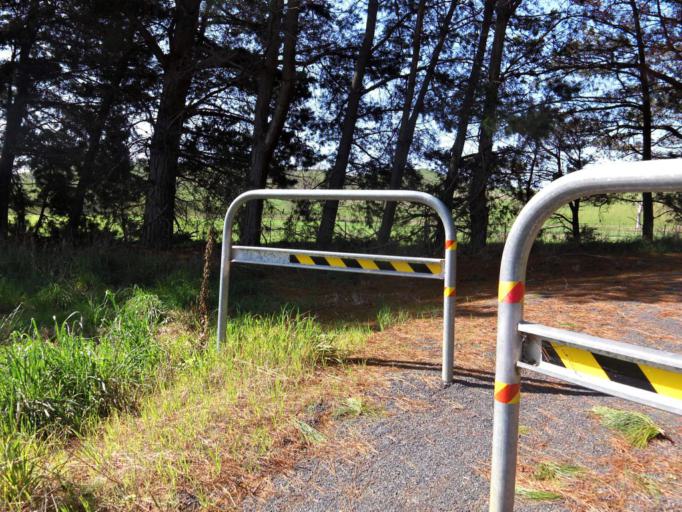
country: AU
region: Victoria
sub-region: Murrindindi
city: Alexandra
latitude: -37.0090
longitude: 145.7533
